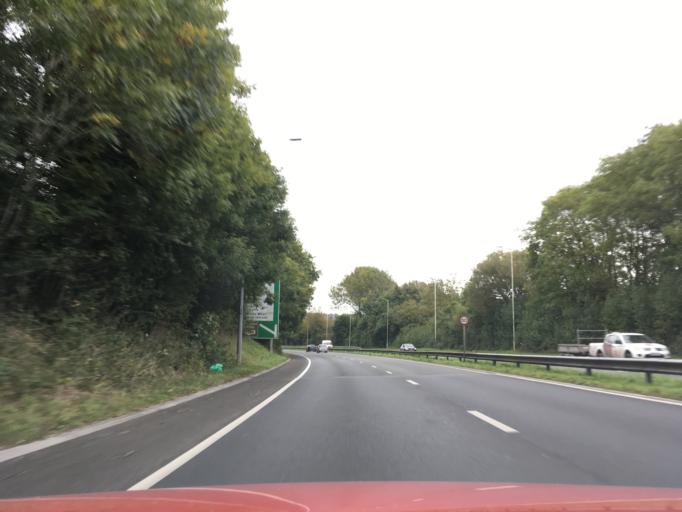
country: GB
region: Wales
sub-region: Cardiff
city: Cardiff
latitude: 51.5028
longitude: -3.1509
